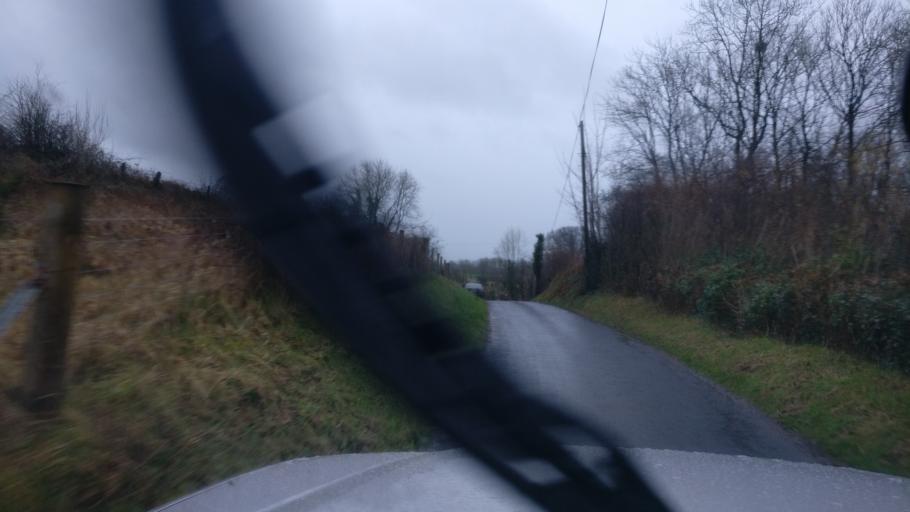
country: IE
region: Connaught
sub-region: County Galway
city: Ballinasloe
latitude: 53.2907
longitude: -8.2775
